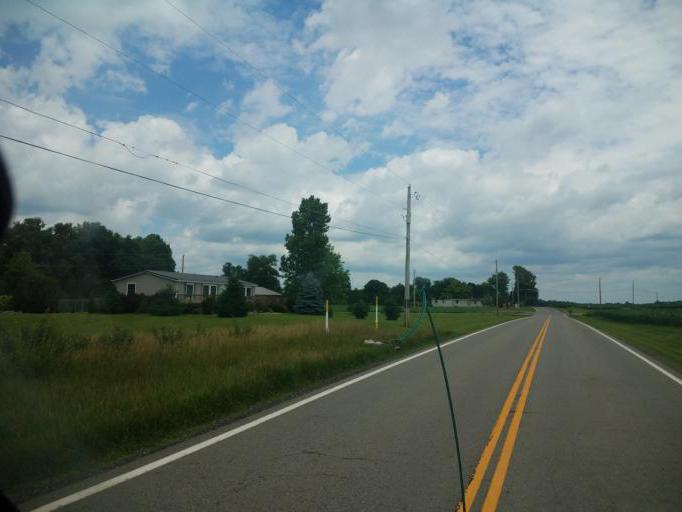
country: US
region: Ohio
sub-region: Huron County
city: Plymouth
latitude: 40.9512
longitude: -82.6973
